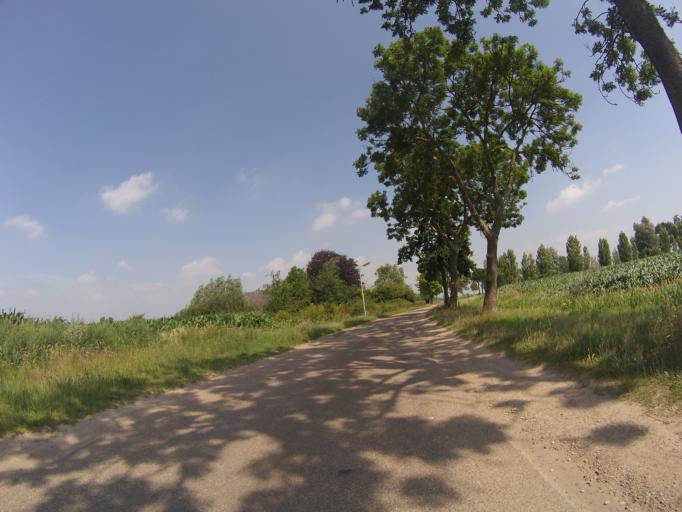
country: NL
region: Utrecht
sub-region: Gemeente Amersfoort
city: Hoogland
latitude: 52.2062
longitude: 5.4157
